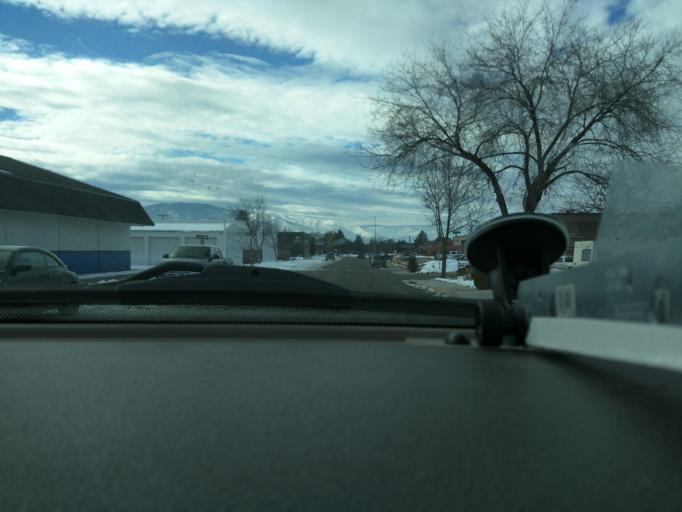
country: US
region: Montana
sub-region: Missoula County
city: Orchard Homes
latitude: 46.8471
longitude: -114.0214
